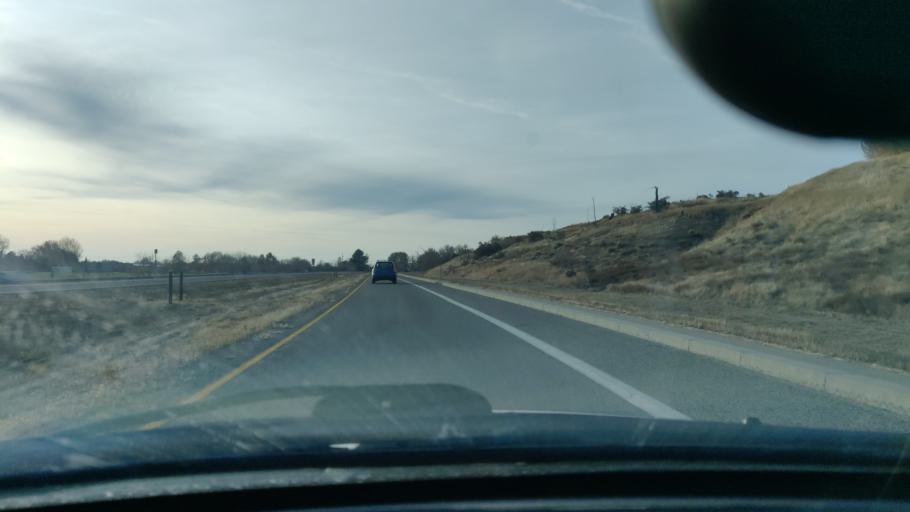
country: US
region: Idaho
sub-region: Ada County
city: Eagle
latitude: 43.6914
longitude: -116.3078
